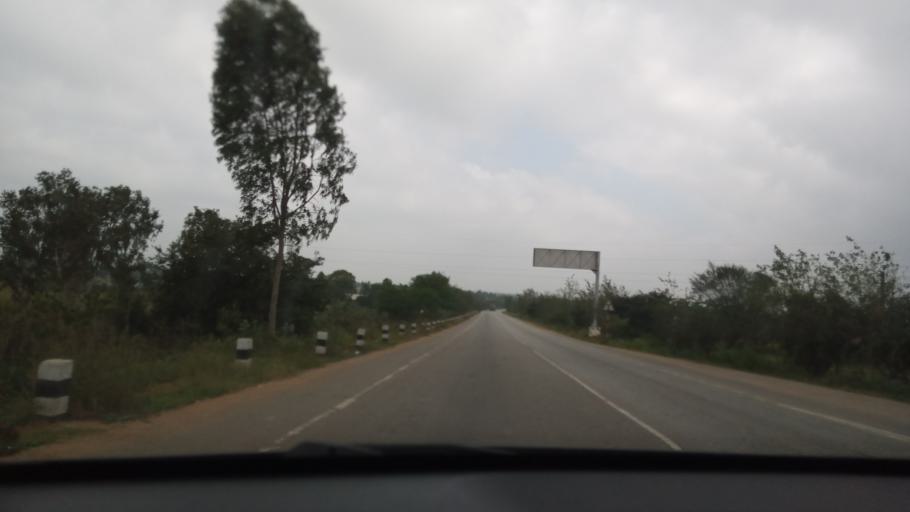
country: IN
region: Karnataka
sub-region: Chikkaballapur
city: Chintamani
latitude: 13.3611
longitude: 78.0418
